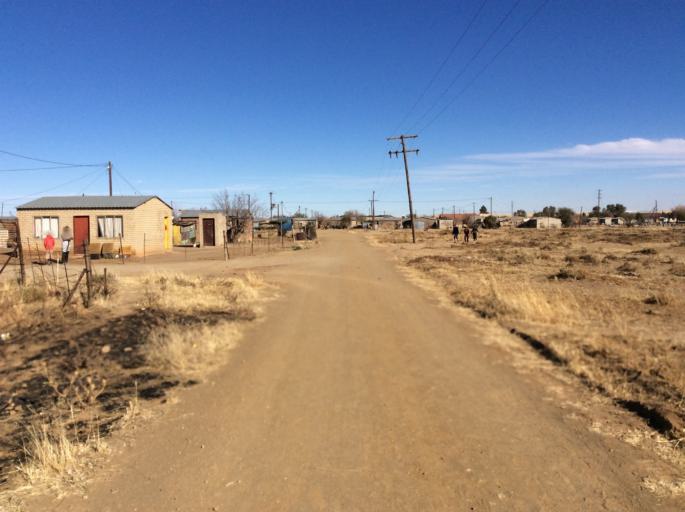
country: ZA
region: Orange Free State
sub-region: Lejweleputswa District Municipality
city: Brandfort
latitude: -28.7308
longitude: 26.1103
